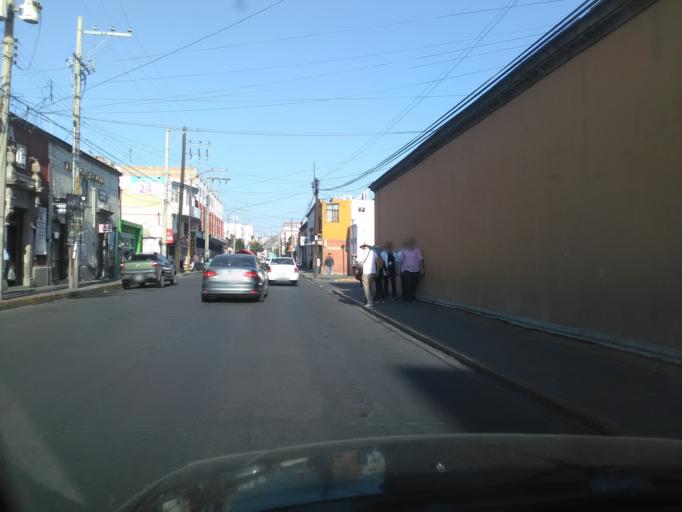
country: MX
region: Durango
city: Victoria de Durango
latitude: 24.0246
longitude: -104.6624
